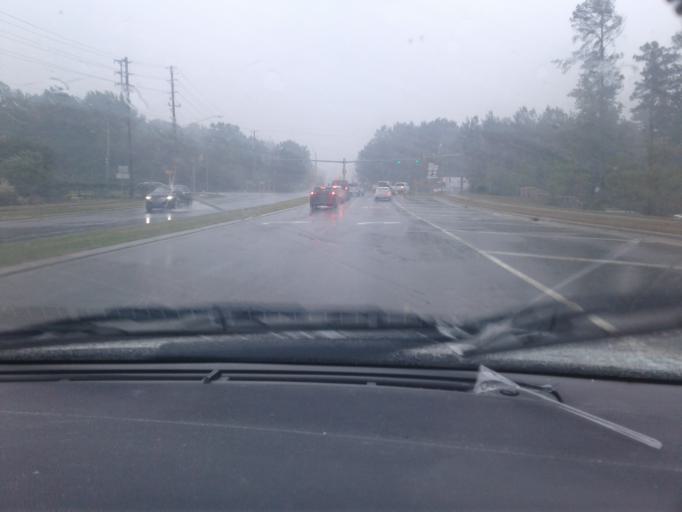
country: US
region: North Carolina
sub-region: Wake County
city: Holly Springs
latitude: 35.6580
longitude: -78.8498
